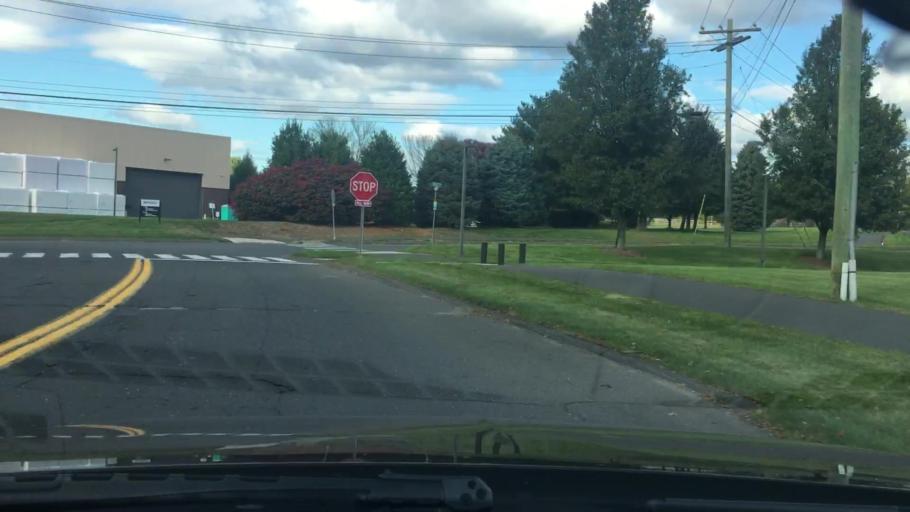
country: US
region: Connecticut
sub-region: Hartford County
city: Plainville
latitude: 41.6980
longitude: -72.8635
